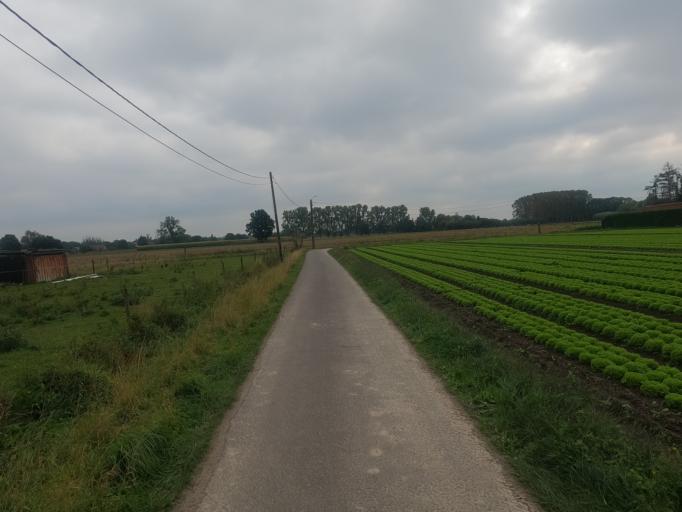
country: BE
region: Flanders
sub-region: Provincie Antwerpen
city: Berlaar
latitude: 51.1075
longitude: 4.6636
